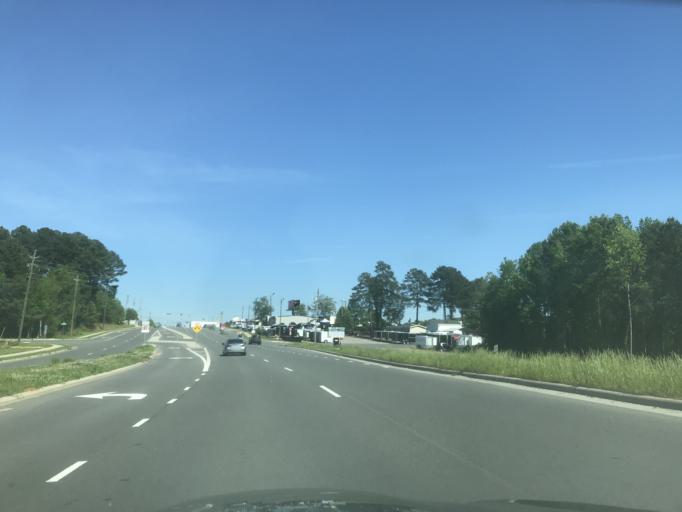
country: US
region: North Carolina
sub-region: Wake County
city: Raleigh
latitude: 35.7313
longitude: -78.6550
